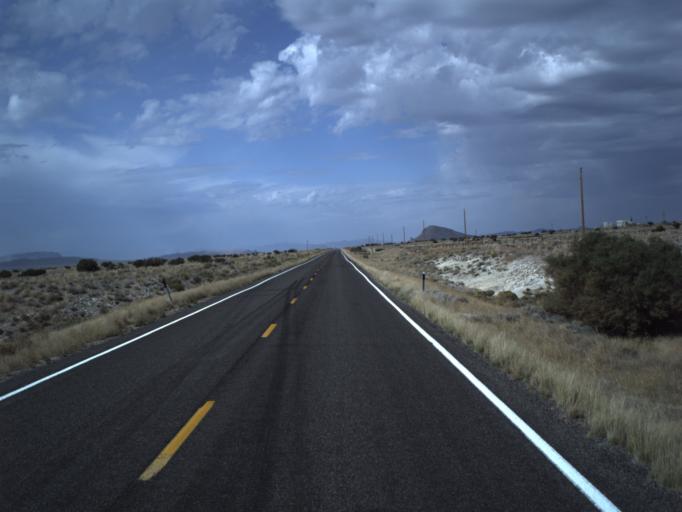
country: US
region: Utah
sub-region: Tooele County
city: Wendover
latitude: 41.4382
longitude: -113.7305
